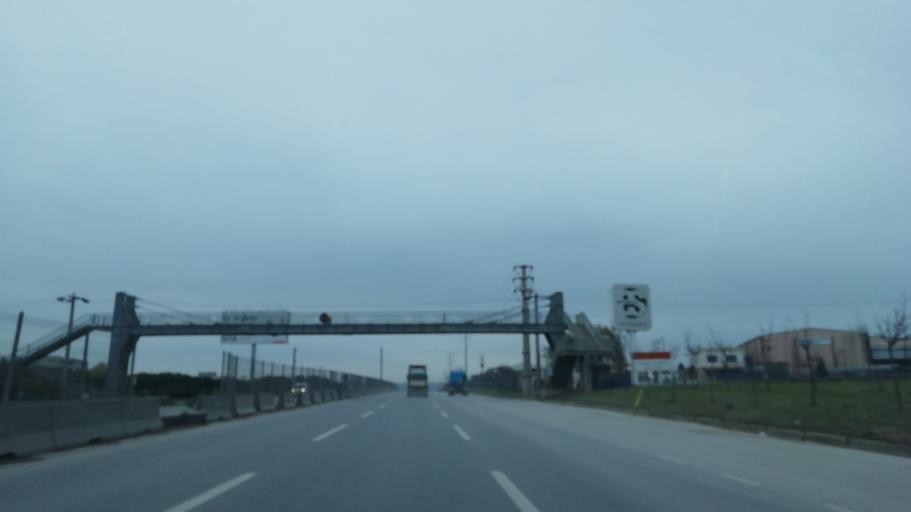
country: TR
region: Kocaeli
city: Tavsanli
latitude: 40.8043
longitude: 29.4843
